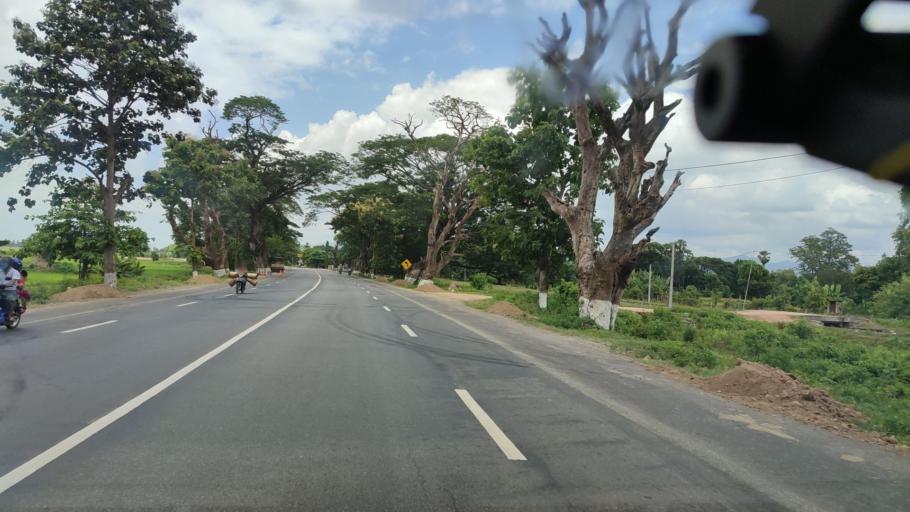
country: MM
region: Mandalay
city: Pyinmana
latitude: 19.7831
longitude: 96.2617
